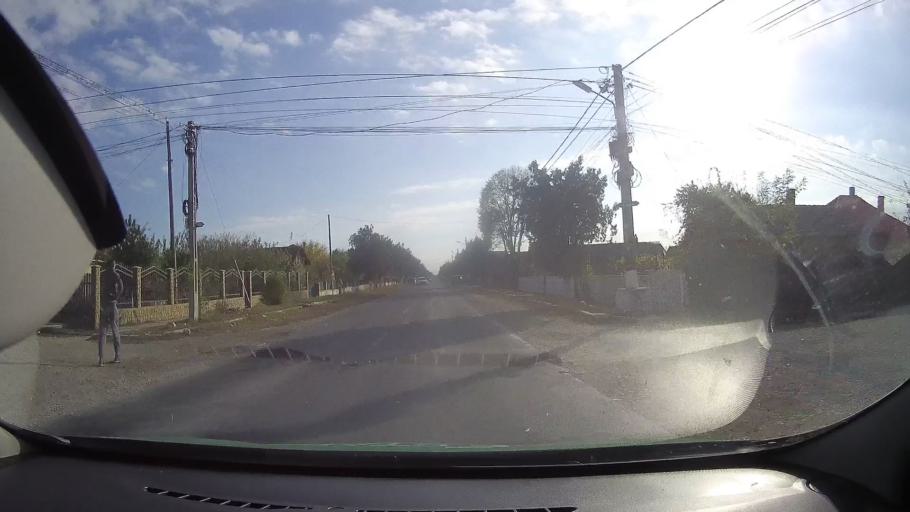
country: RO
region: Constanta
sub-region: Comuna Corbu
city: Corbu
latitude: 44.3925
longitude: 28.6620
